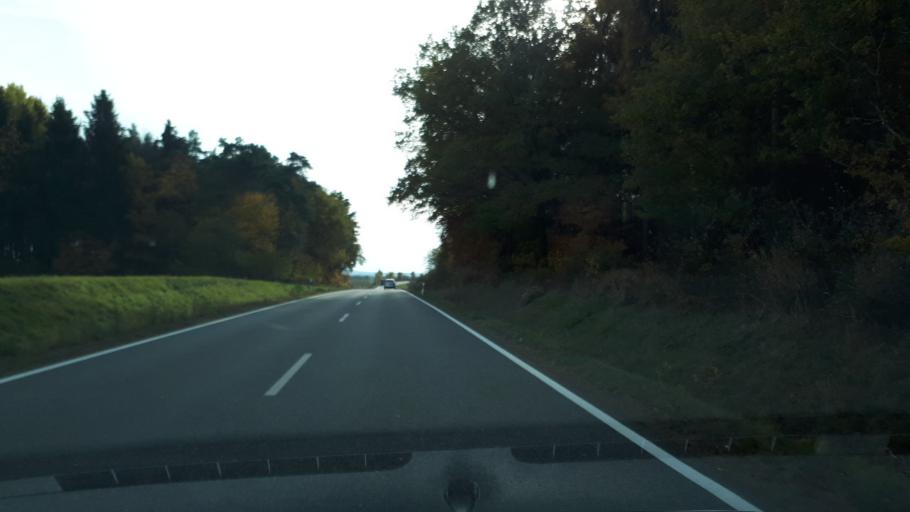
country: DE
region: Rheinland-Pfalz
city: Gillenbeuren
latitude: 50.1446
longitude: 7.0317
